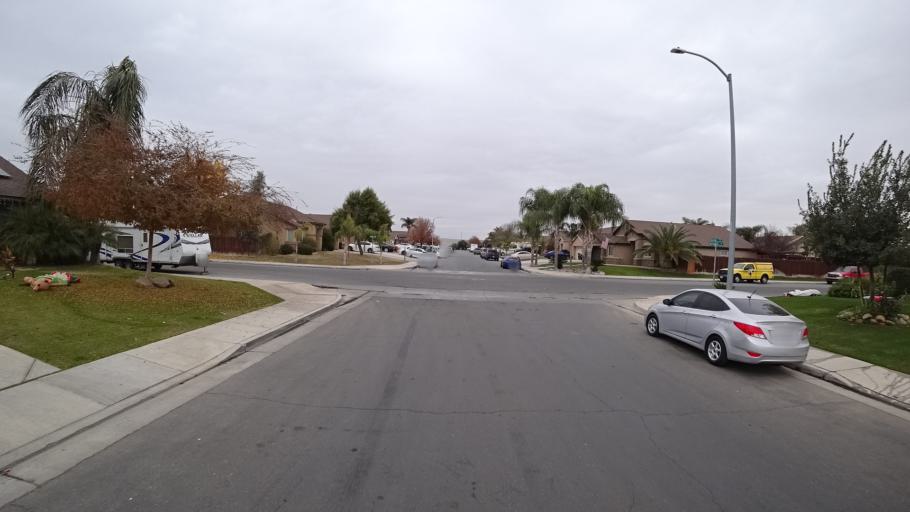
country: US
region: California
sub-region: Kern County
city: Greenfield
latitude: 35.2861
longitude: -119.0303
